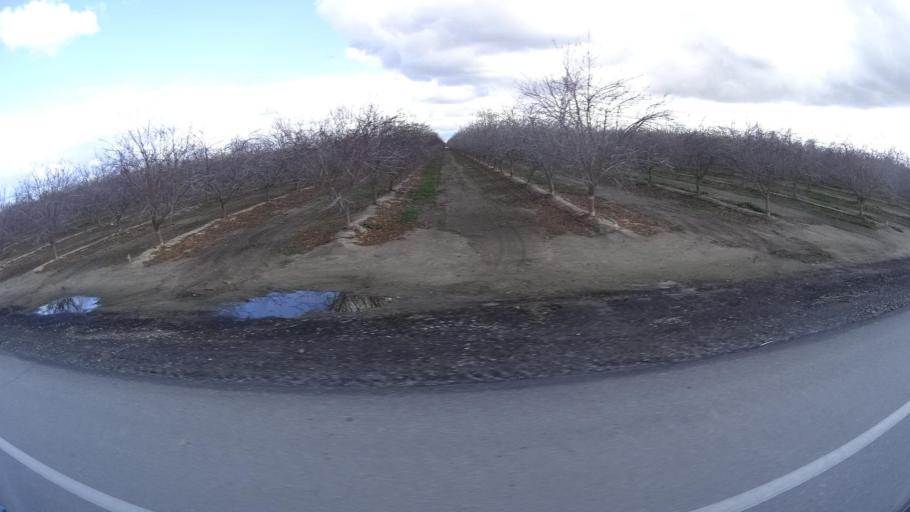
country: US
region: California
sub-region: Kern County
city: Greenfield
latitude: 35.2157
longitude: -119.1099
